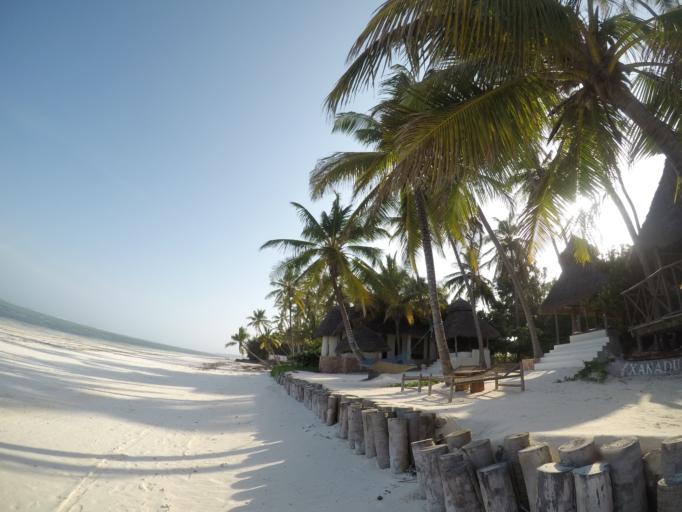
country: TZ
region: Zanzibar Central/South
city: Nganane
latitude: -6.2031
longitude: 39.5350
